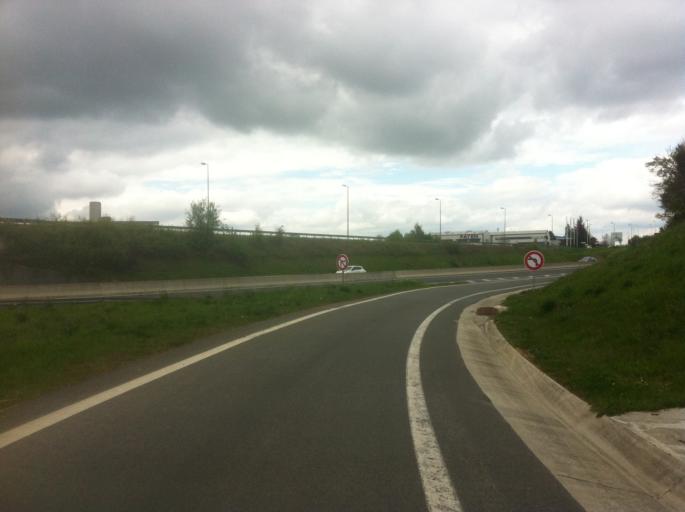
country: FR
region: Picardie
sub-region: Departement de l'Oise
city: Nanteuil-le-Haudouin
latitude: 49.1378
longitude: 2.7992
